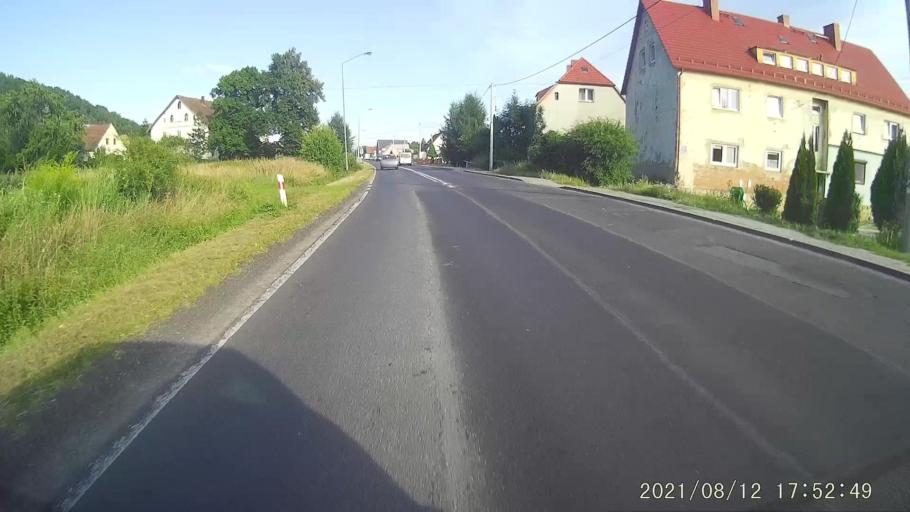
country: PL
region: Lower Silesian Voivodeship
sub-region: Powiat klodzki
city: Klodzko
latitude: 50.3696
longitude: 16.6771
